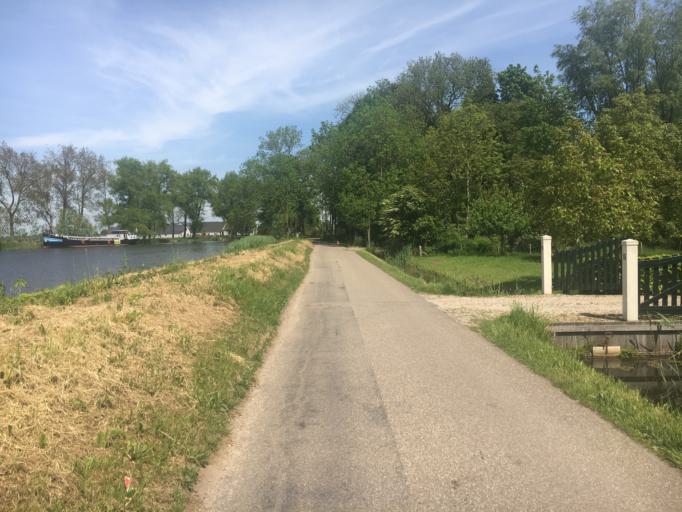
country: NL
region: Utrecht
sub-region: Stichtse Vecht
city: Vreeland
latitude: 52.2369
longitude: 5.0342
